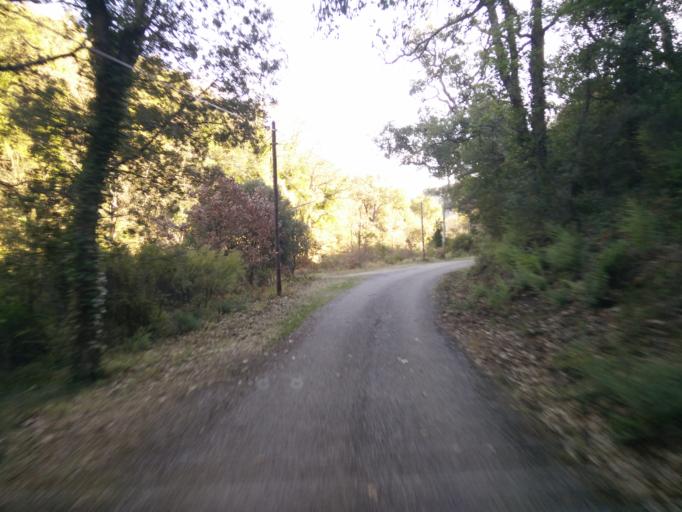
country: FR
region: Provence-Alpes-Cote d'Azur
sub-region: Departement du Var
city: Collobrieres
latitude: 43.2555
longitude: 6.3072
